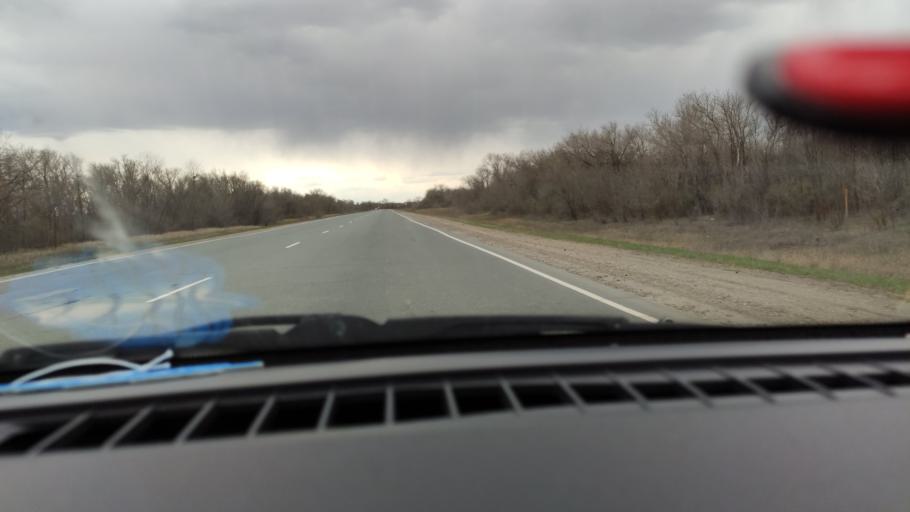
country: RU
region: Saratov
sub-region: Saratovskiy Rayon
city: Saratov
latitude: 51.7093
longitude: 46.0169
